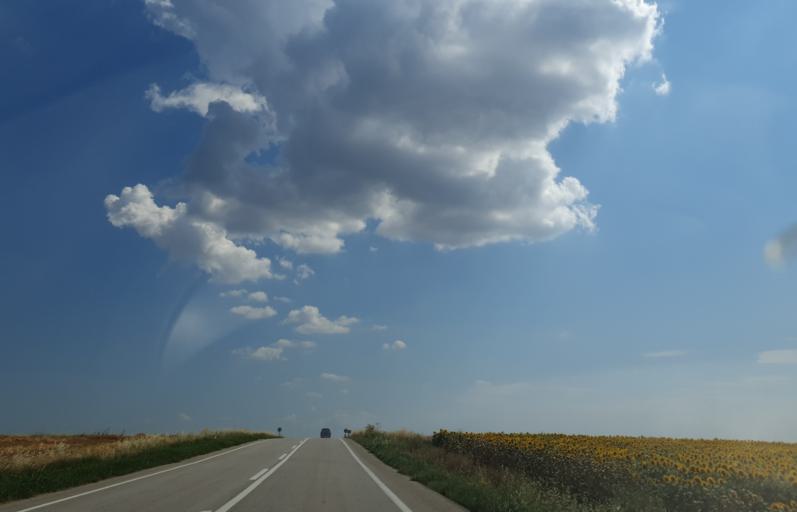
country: TR
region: Kirklareli
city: Buyukkaristiran
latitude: 41.4122
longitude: 27.5775
